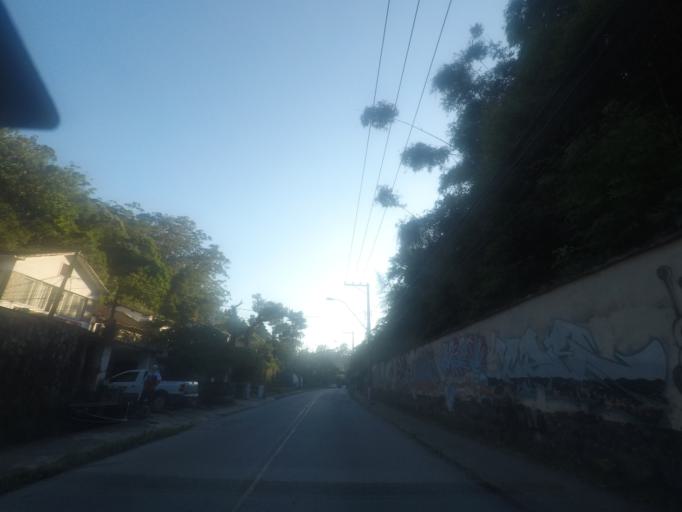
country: BR
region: Rio de Janeiro
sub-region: Petropolis
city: Petropolis
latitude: -22.5261
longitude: -43.1871
